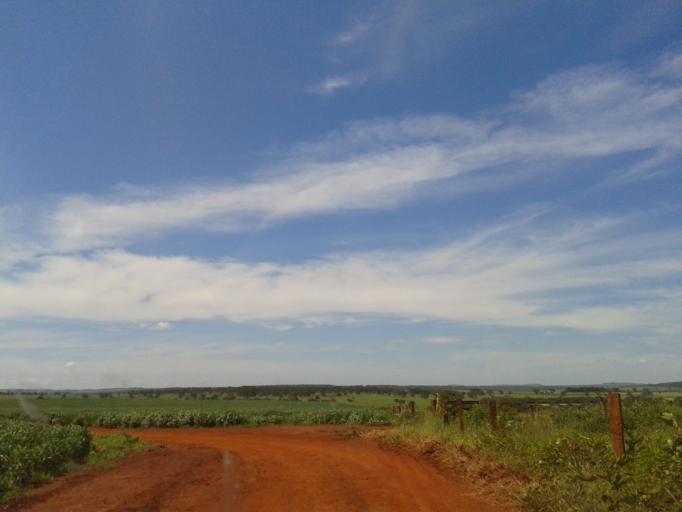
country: BR
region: Minas Gerais
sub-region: Capinopolis
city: Capinopolis
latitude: -18.7731
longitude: -49.8093
